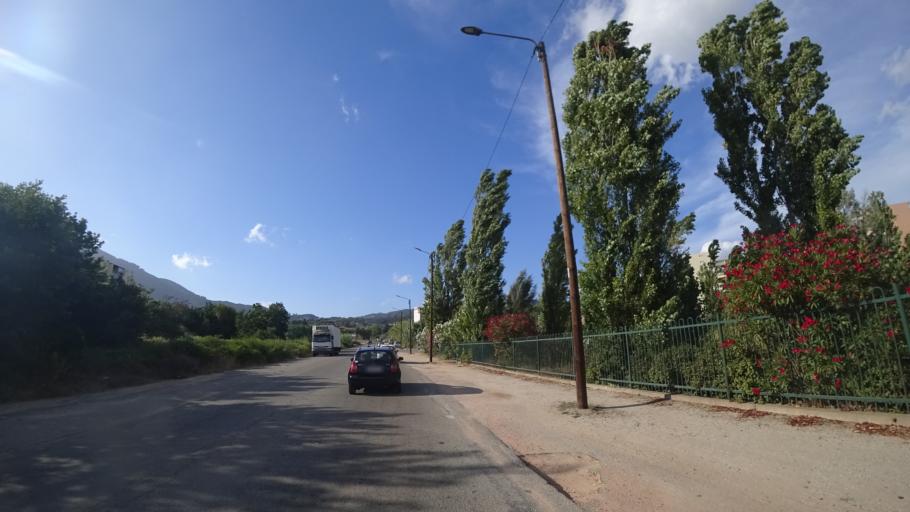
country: FR
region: Corsica
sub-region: Departement de la Corse-du-Sud
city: Ajaccio
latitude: 41.9370
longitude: 8.7426
